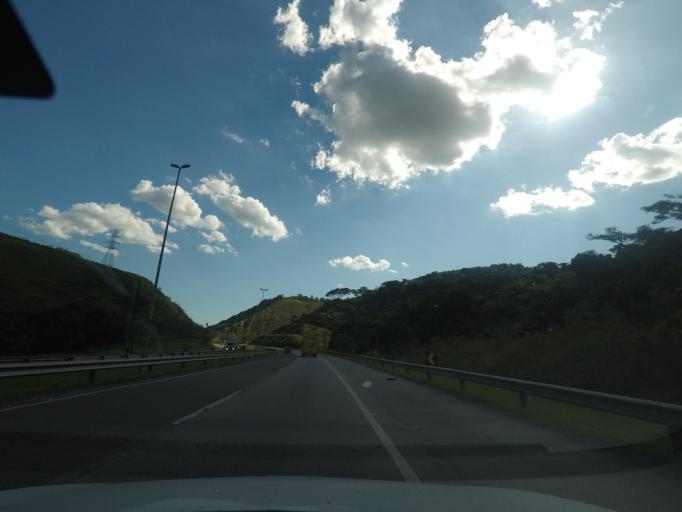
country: BR
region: Rio de Janeiro
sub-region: Guapimirim
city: Guapimirim
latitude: -22.5727
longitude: -43.0081
